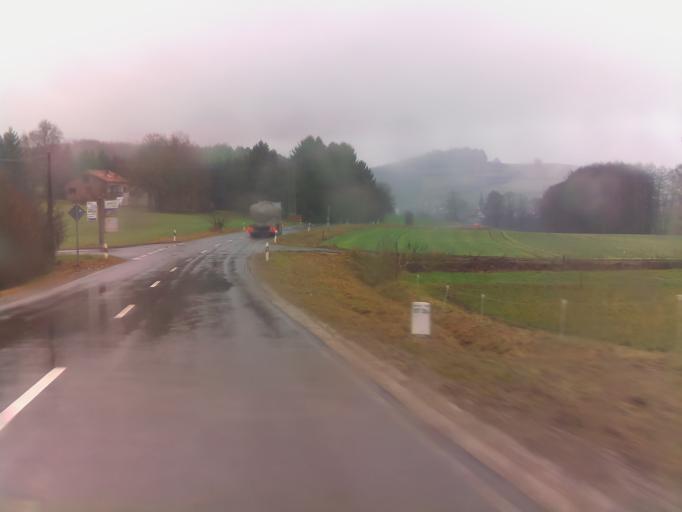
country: DE
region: Hesse
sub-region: Regierungsbezirk Kassel
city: Dipperz
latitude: 50.5167
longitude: 9.8203
